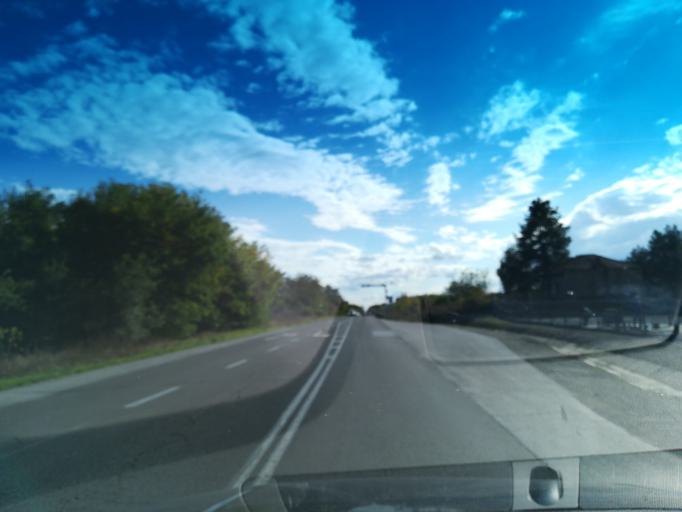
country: BG
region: Stara Zagora
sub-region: Obshtina Stara Zagora
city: Stara Zagora
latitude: 42.3604
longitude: 25.6560
